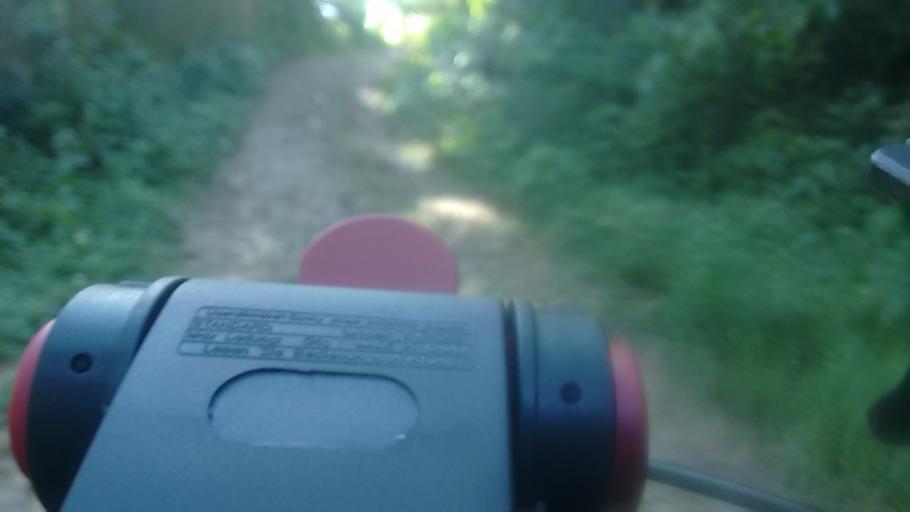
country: IN
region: Kerala
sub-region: Thrissur District
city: Chelakara
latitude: 10.6332
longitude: 76.3055
